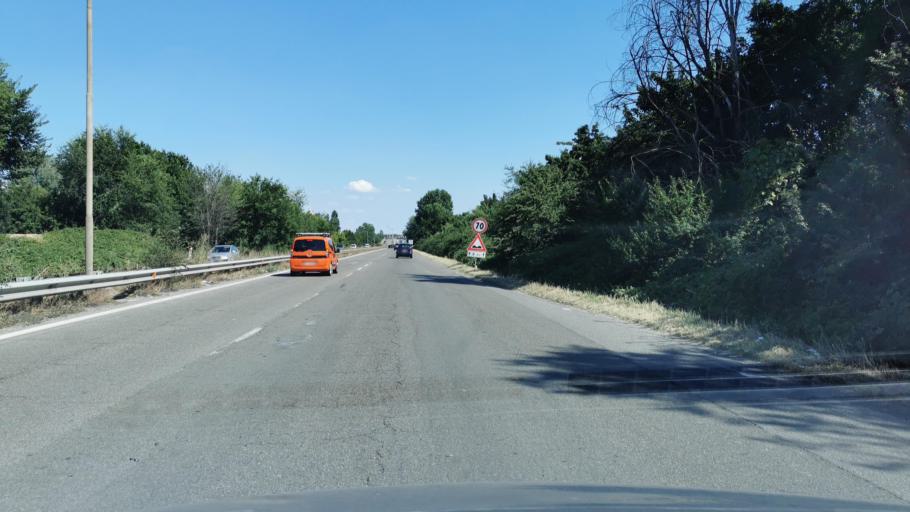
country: IT
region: Emilia-Romagna
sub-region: Provincia di Modena
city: Modena
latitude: 44.6681
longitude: 10.9310
